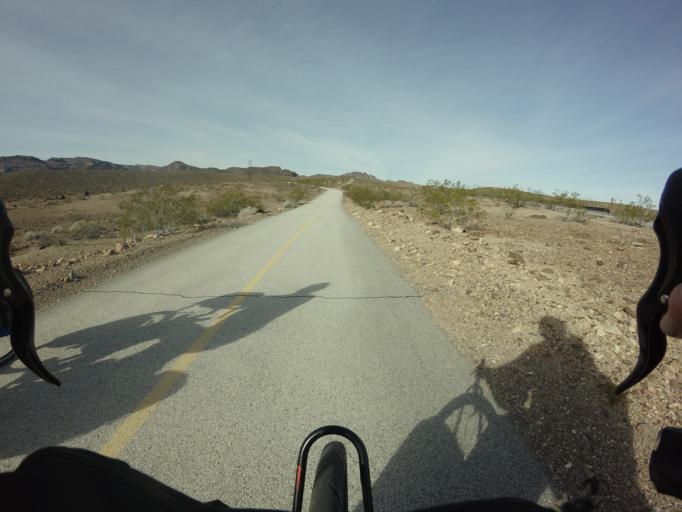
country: US
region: Nevada
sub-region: Clark County
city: Boulder City
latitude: 36.0765
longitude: -114.8150
